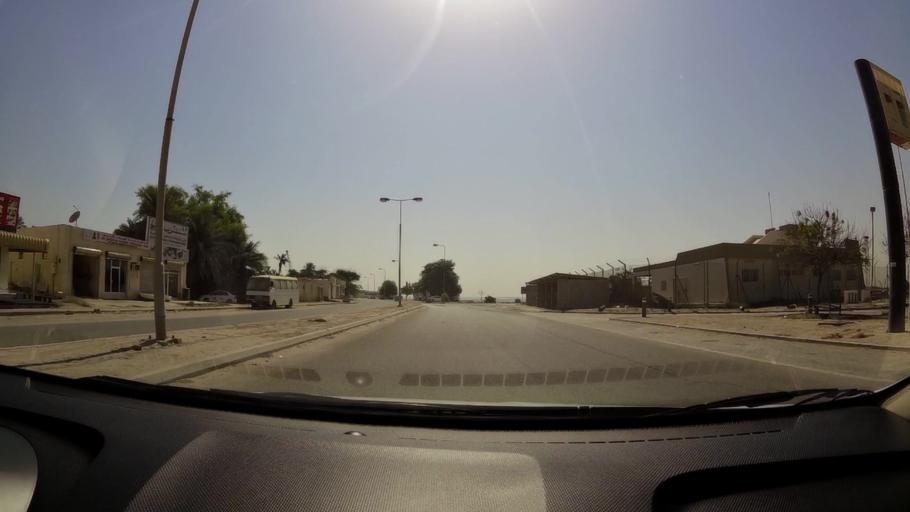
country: AE
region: Umm al Qaywayn
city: Umm al Qaywayn
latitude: 25.5819
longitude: 55.5750
